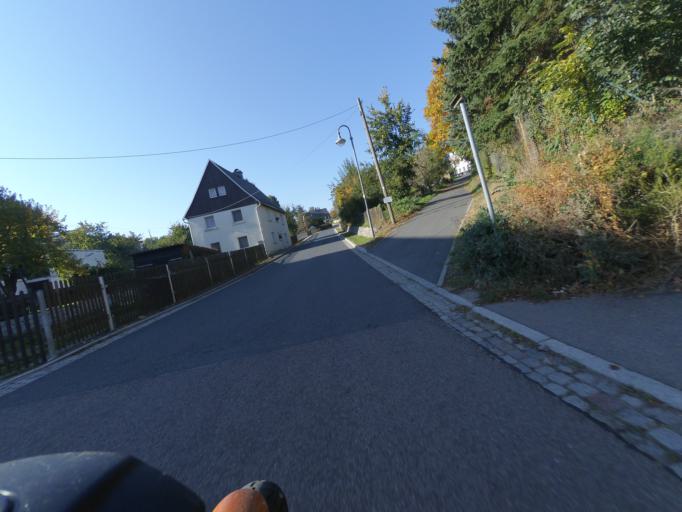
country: DE
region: Saxony
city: Rabenau
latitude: 50.9391
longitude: 13.6112
